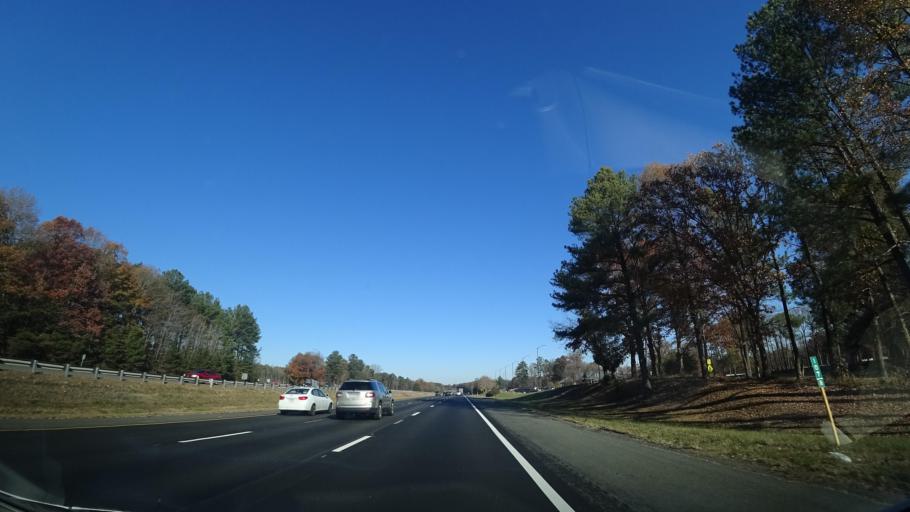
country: US
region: Virginia
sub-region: Caroline County
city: Bowling Green
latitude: 37.9792
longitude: -77.4916
